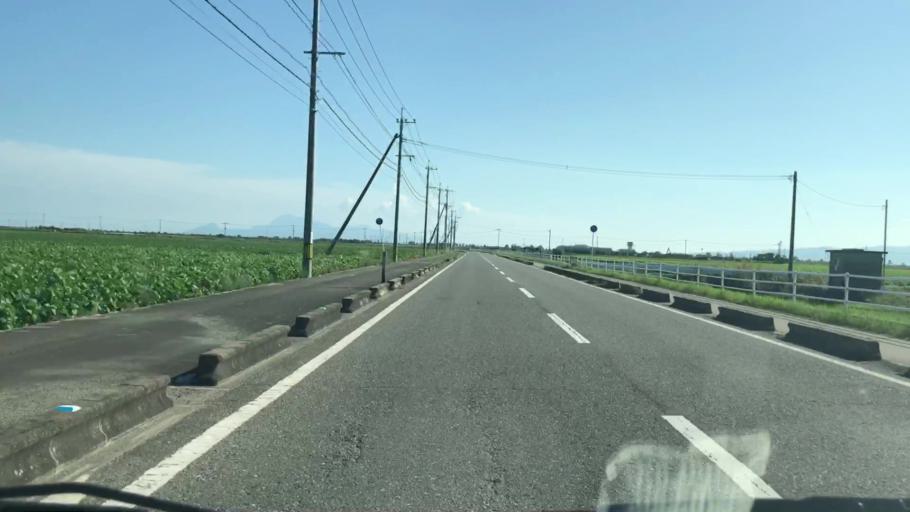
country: JP
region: Saga Prefecture
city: Okawa
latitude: 33.1689
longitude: 130.3100
